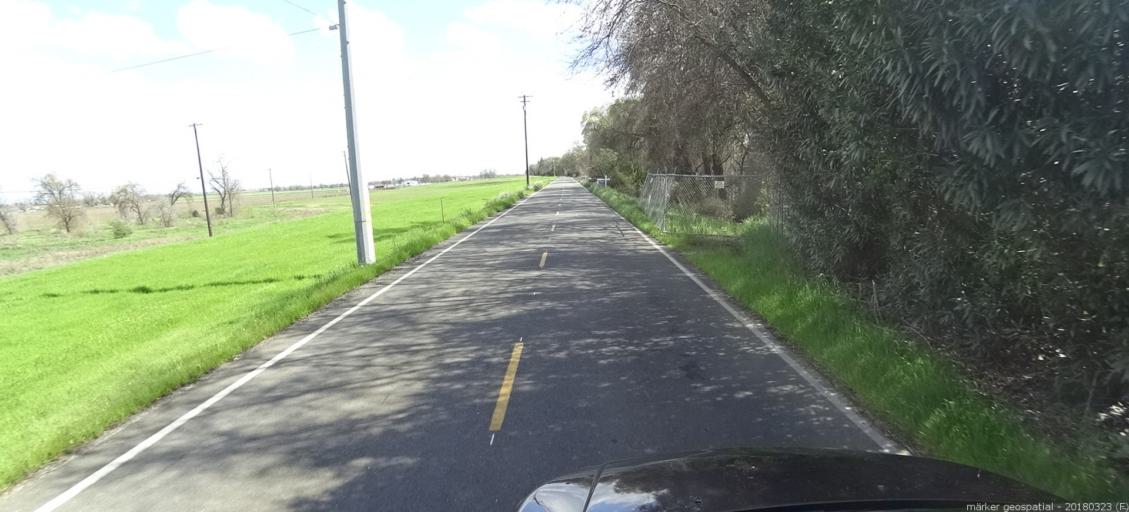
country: US
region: California
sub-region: Yolo County
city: West Sacramento
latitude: 38.6723
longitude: -121.6229
